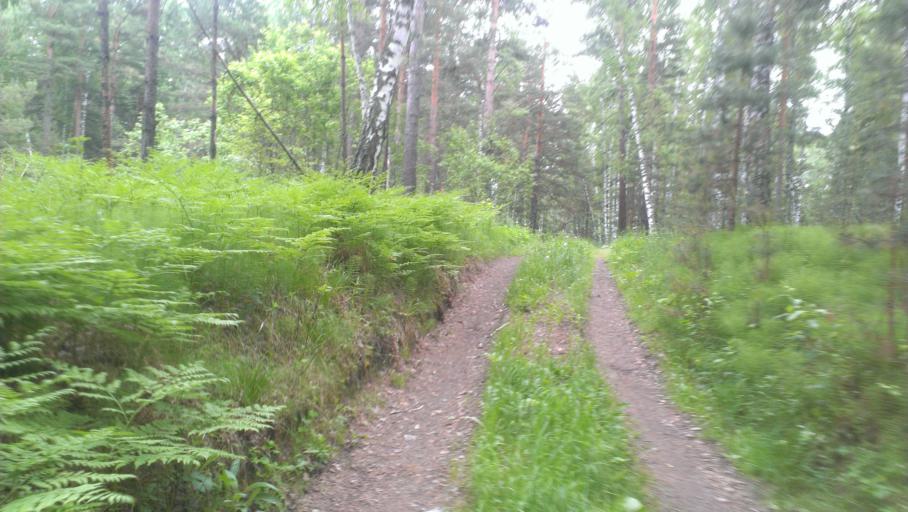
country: RU
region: Altai Krai
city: Sannikovo
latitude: 53.3428
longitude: 84.0454
